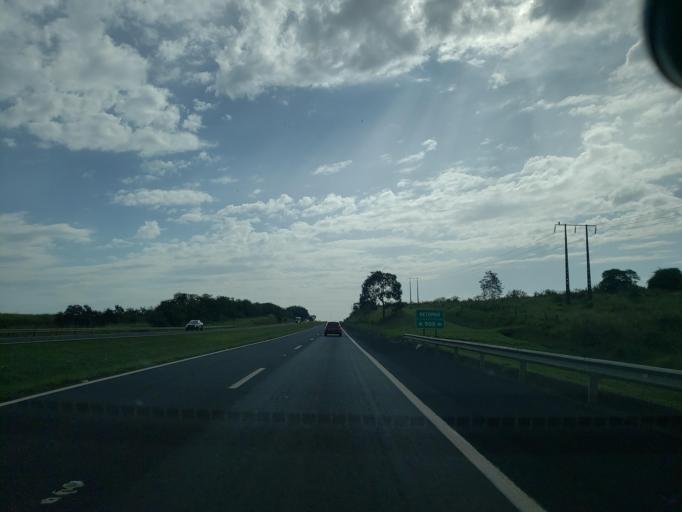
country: BR
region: Sao Paulo
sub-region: Lins
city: Lins
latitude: -21.7409
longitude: -49.6984
